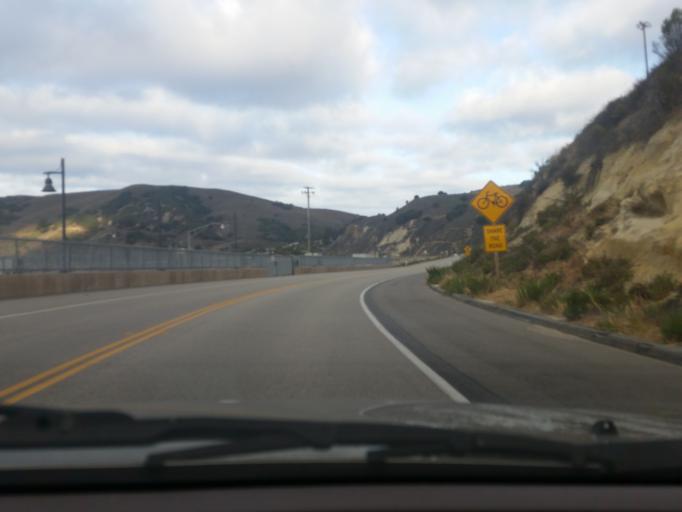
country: US
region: California
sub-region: San Luis Obispo County
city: Avila Beach
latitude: 35.1782
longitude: -120.7406
